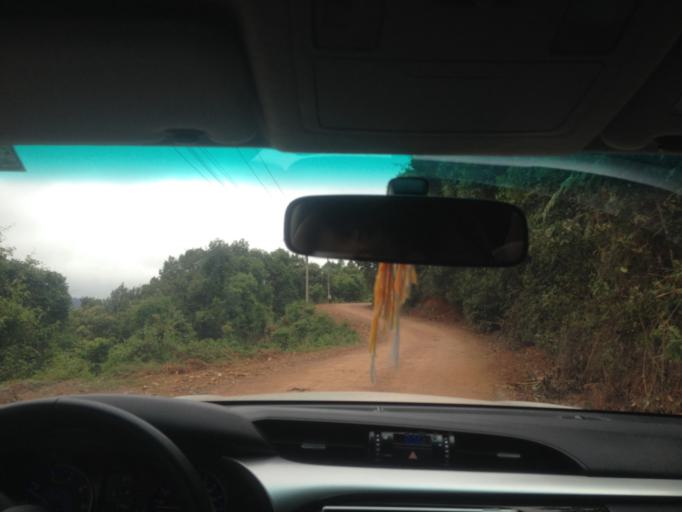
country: TH
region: Nan
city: Chaloem Phra Kiat
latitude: 19.9770
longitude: 101.1358
